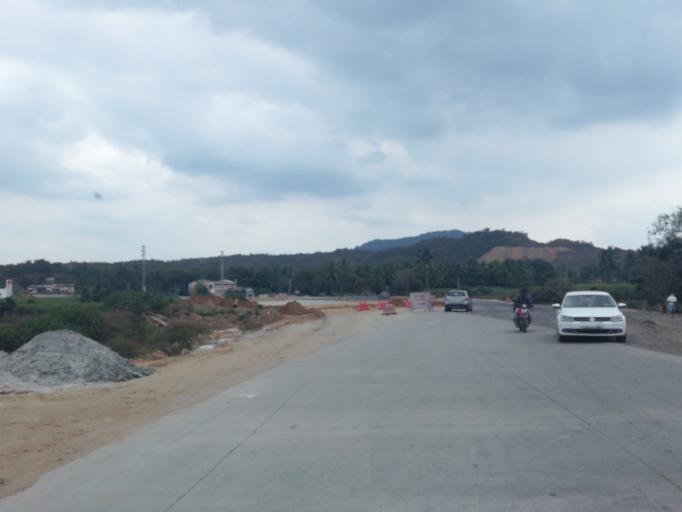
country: IN
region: Andhra Pradesh
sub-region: Chittoor
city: Ramapuram
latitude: 13.0984
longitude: 79.1254
